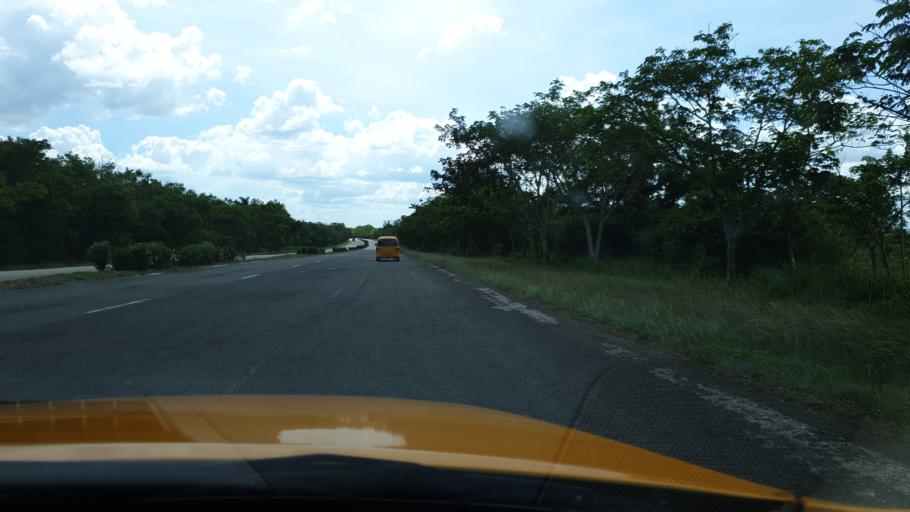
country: CU
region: Cienfuegos
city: Cruces
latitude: 22.4543
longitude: -80.2988
